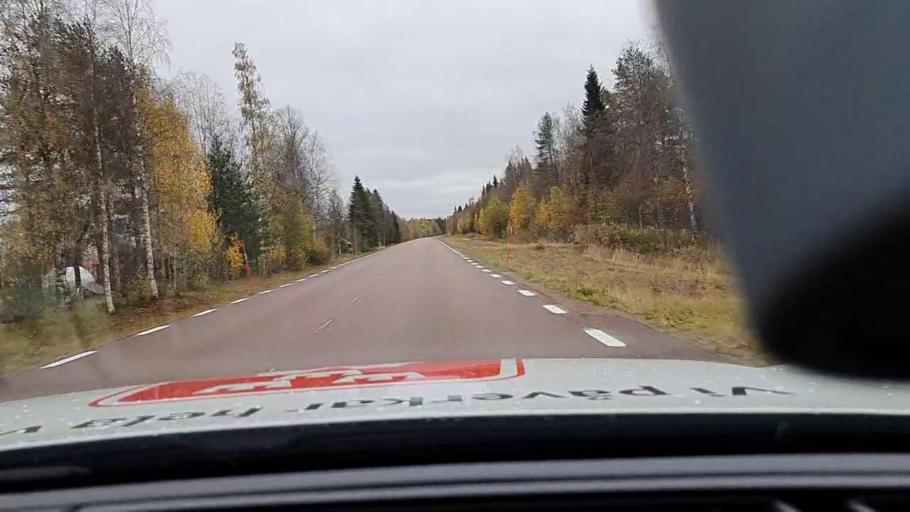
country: FI
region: Lapland
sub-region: Kemi-Tornio
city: Tornio
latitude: 66.0540
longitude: 23.9367
